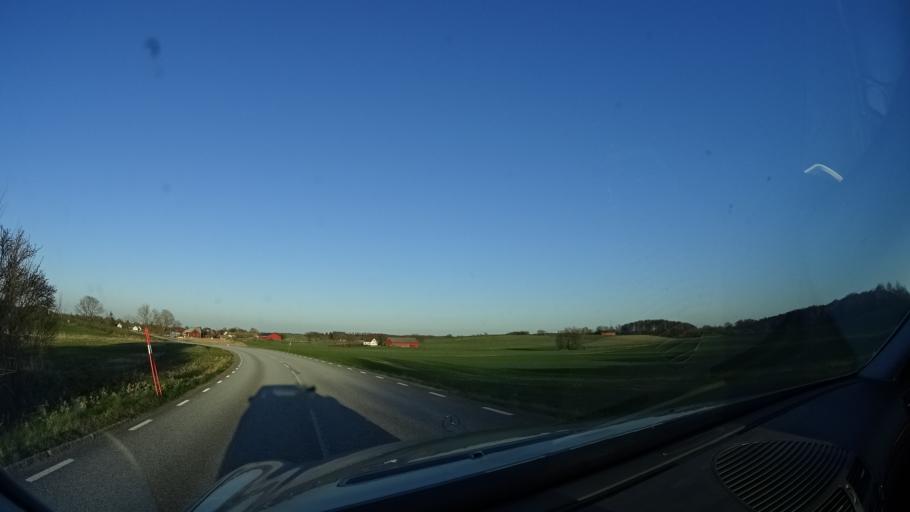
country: SE
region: Skane
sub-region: Klippans Kommun
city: Ljungbyhed
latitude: 55.9625
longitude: 13.2315
